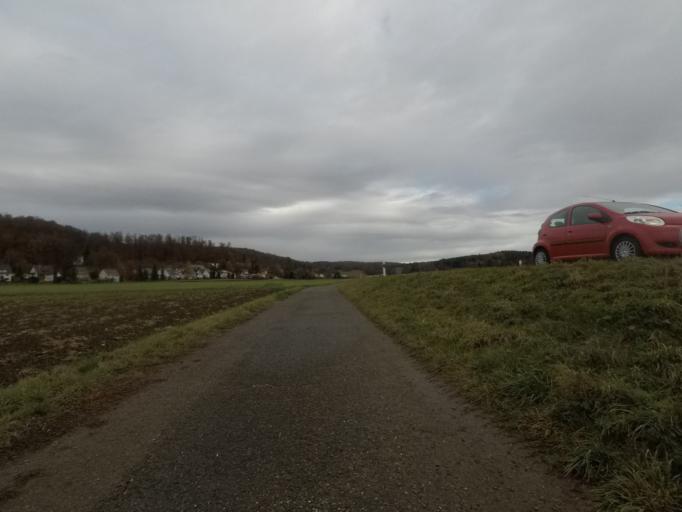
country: DE
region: Baden-Wuerttemberg
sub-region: Tuebingen Region
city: Pfullingen
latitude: 48.4010
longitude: 9.2770
